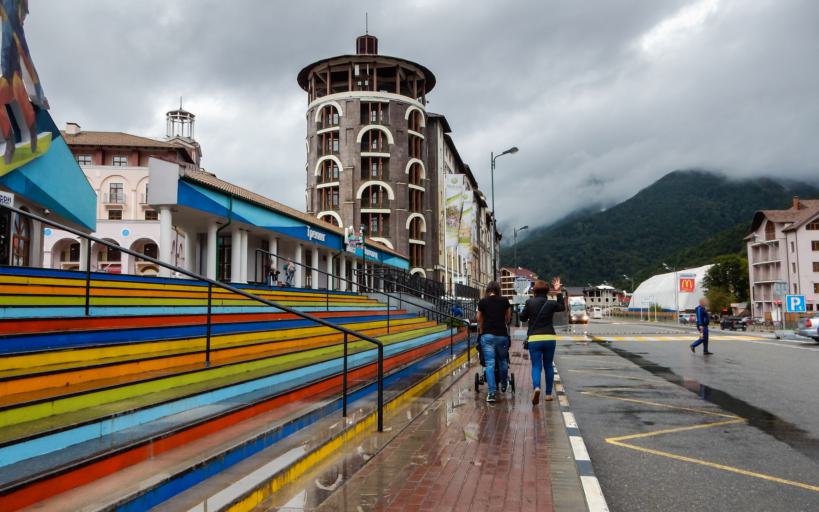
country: RU
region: Krasnodarskiy
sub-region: Sochi City
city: Krasnaya Polyana
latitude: 43.6835
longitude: 40.2671
